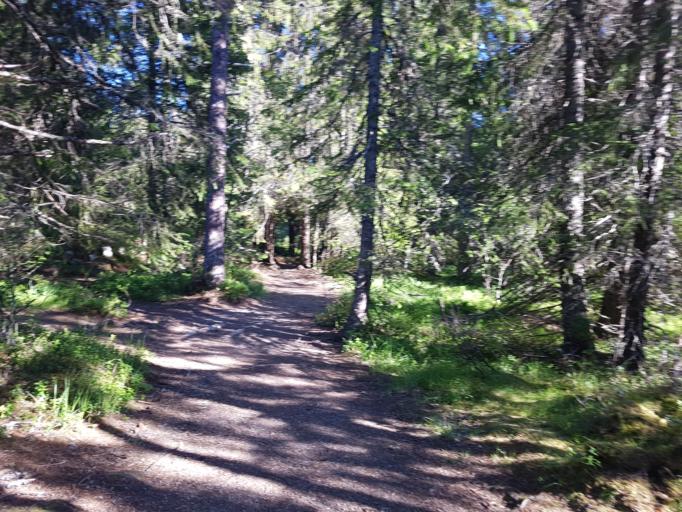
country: NO
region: Sor-Trondelag
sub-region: Trondheim
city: Trondheim
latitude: 63.4218
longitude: 10.3007
